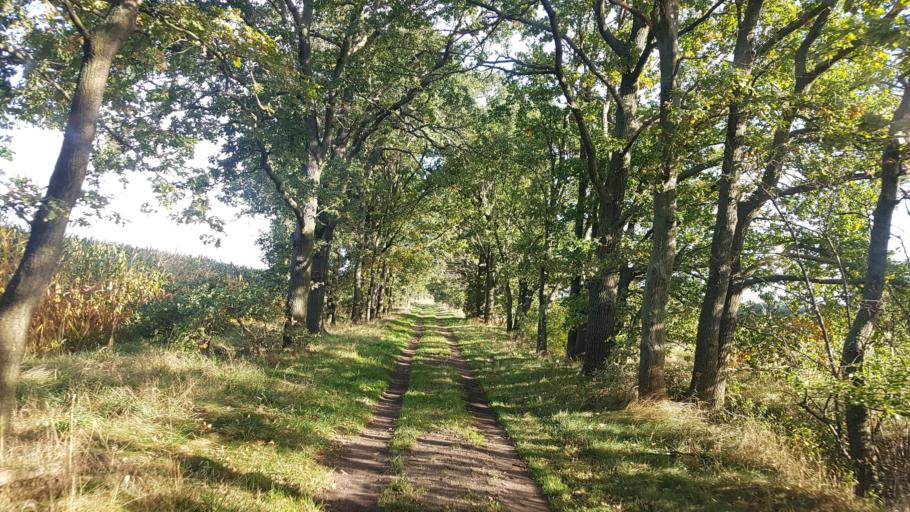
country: DE
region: Brandenburg
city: Schraden
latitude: 51.4248
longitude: 13.7156
